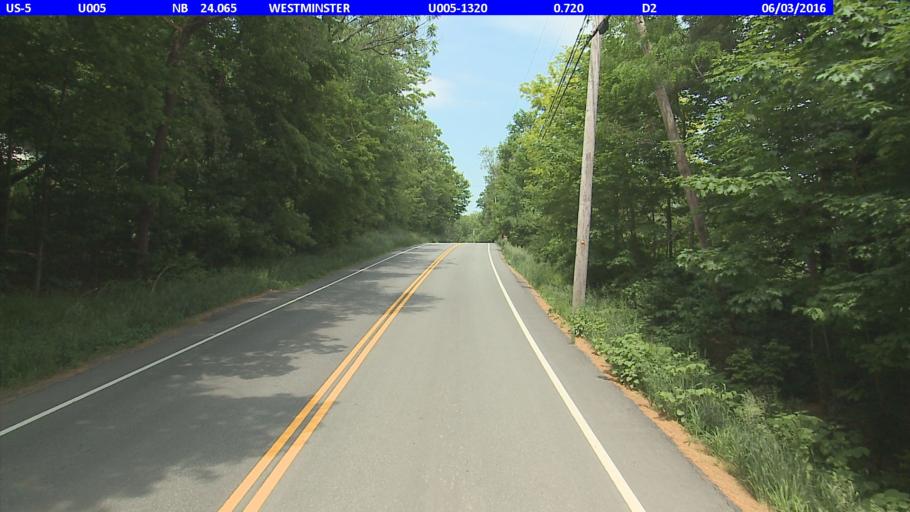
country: US
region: New Hampshire
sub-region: Cheshire County
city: Westmoreland
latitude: 43.0307
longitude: -72.4675
